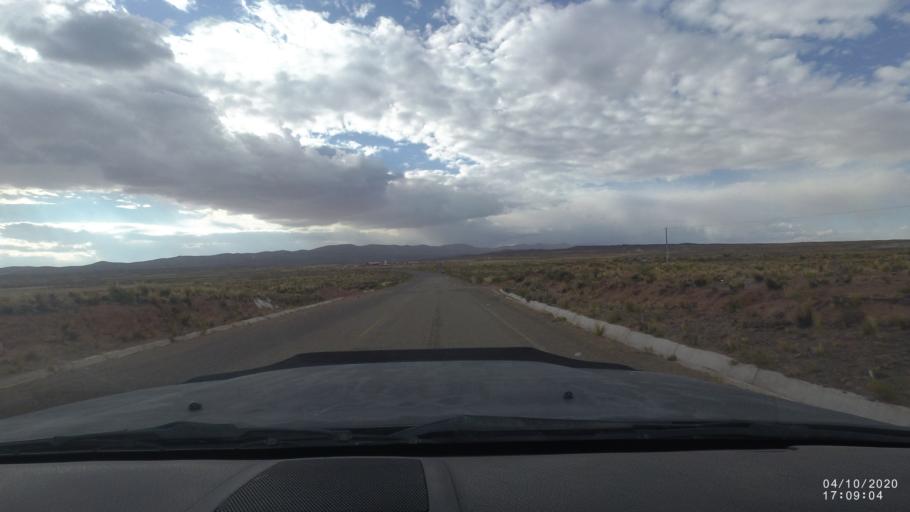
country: BO
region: Oruro
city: Oruro
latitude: -18.3423
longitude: -67.5789
